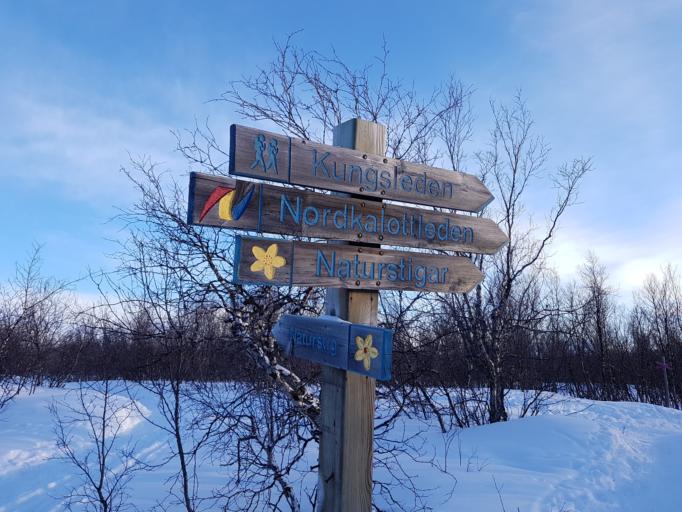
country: NO
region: Troms
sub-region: Bardu
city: Setermoen
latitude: 68.3573
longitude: 18.7766
